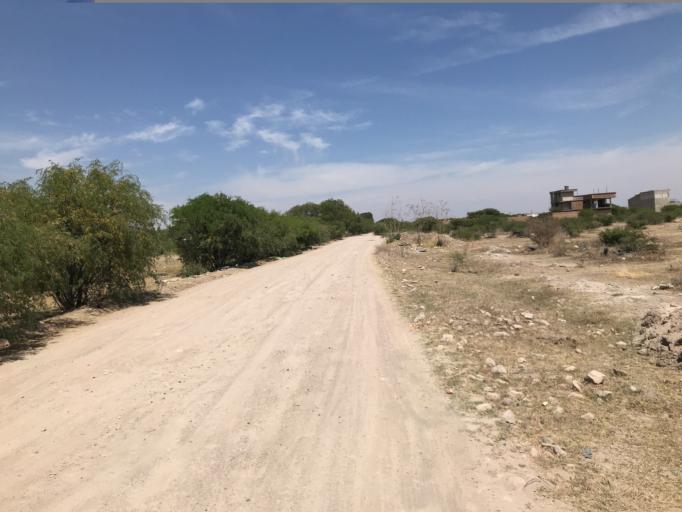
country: MX
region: Durango
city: Victoria de Durango
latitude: 23.9802
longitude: -104.6880
